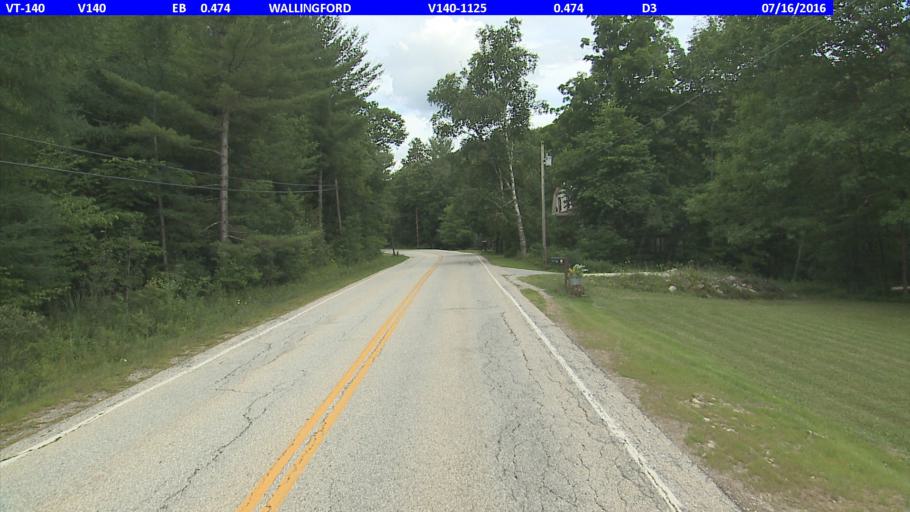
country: US
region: Vermont
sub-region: Rutland County
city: Rutland
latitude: 43.4691
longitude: -72.9688
